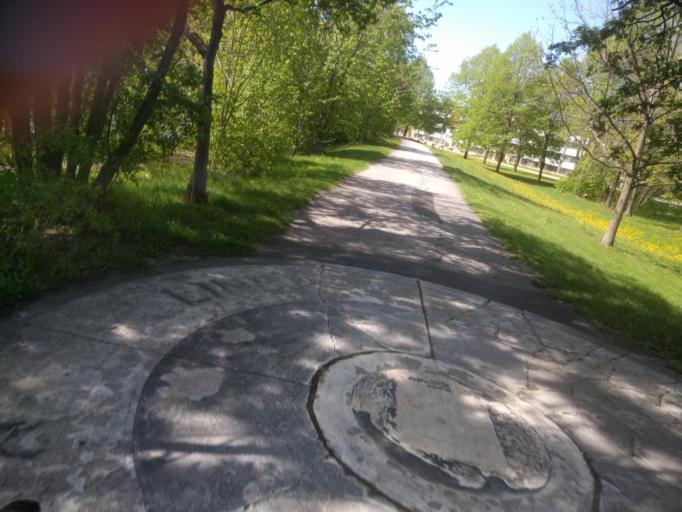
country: CA
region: Ontario
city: Ottawa
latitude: 45.3931
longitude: -75.6765
